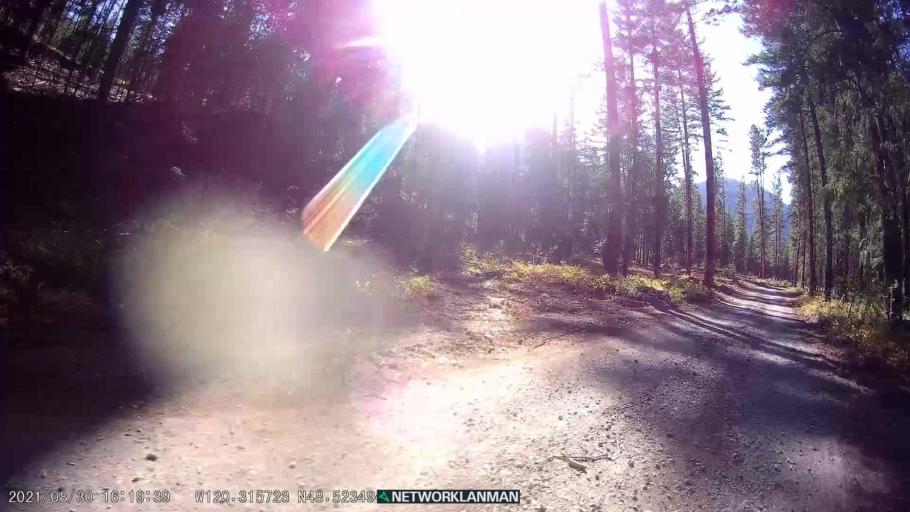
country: US
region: Washington
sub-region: Chelan County
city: Granite Falls
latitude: 48.5235
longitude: -120.3157
